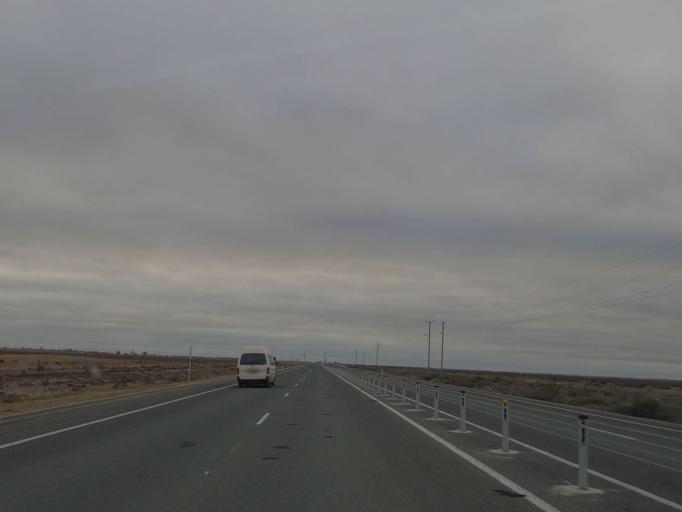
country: AU
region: Victoria
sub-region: Swan Hill
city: Swan Hill
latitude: -35.5135
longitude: 143.7263
